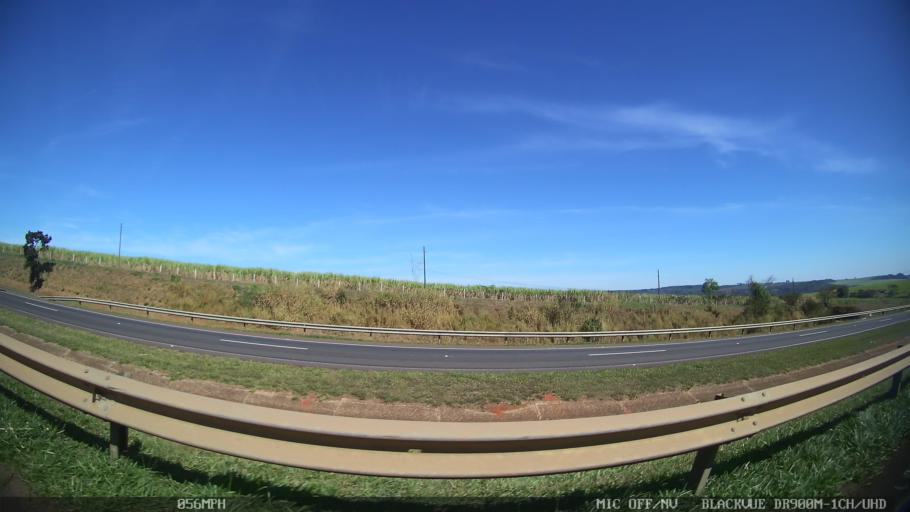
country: BR
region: Sao Paulo
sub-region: Santa Rita Do Passa Quatro
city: Santa Rita do Passa Quatro
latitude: -21.7707
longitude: -47.5453
